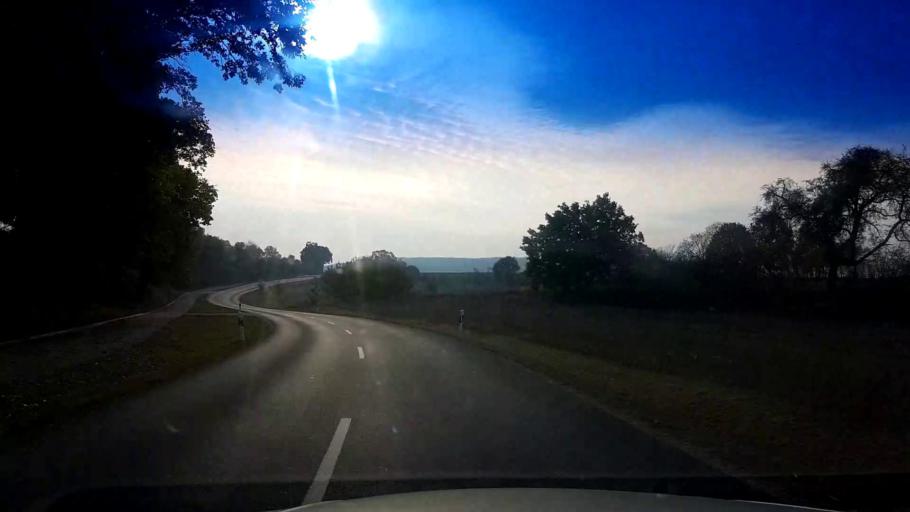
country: DE
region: Bavaria
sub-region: Upper Franconia
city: Altenkunstadt
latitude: 50.1215
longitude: 11.2618
